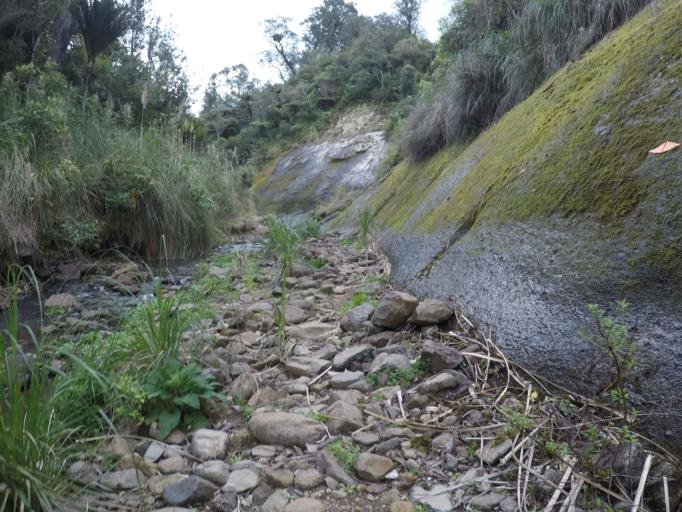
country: NZ
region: Bay of Plenty
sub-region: Western Bay of Plenty District
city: Waihi Beach
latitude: -37.3802
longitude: 175.9296
